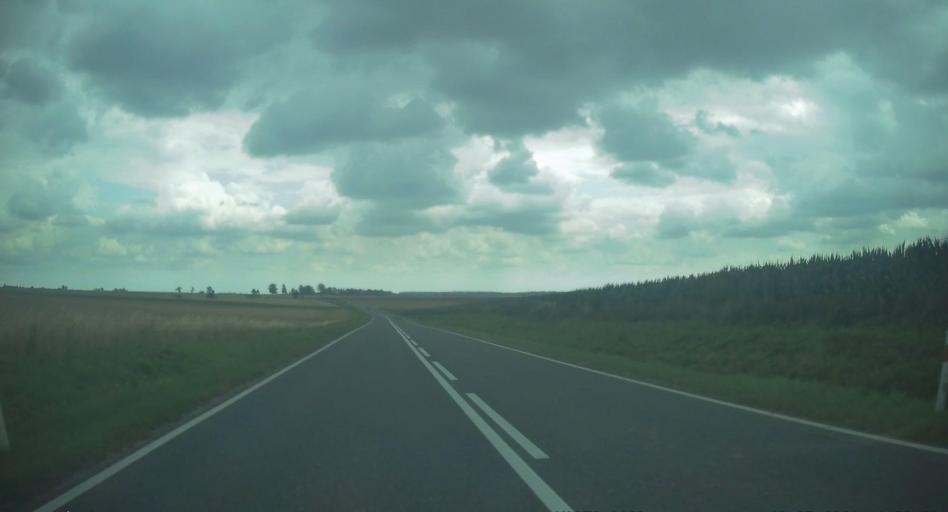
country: PL
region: Opole Voivodeship
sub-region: Powiat prudnicki
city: Moszczanka
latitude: 50.4216
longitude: 17.4655
